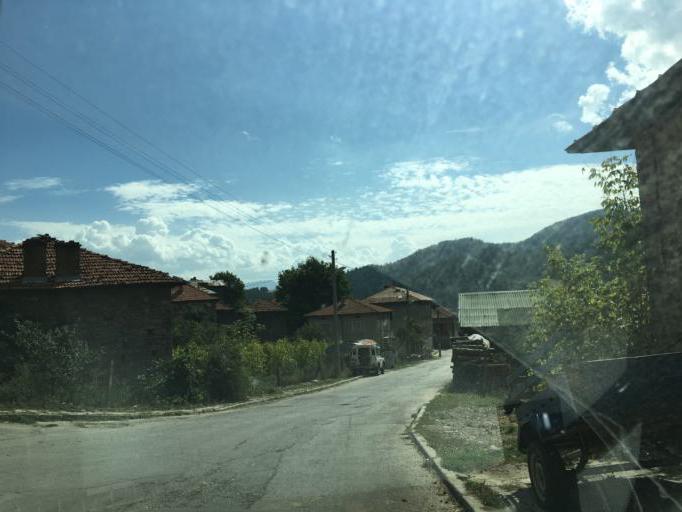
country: BG
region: Pazardzhik
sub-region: Obshtina Bratsigovo
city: Bratsigovo
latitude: 41.8852
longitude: 24.3480
